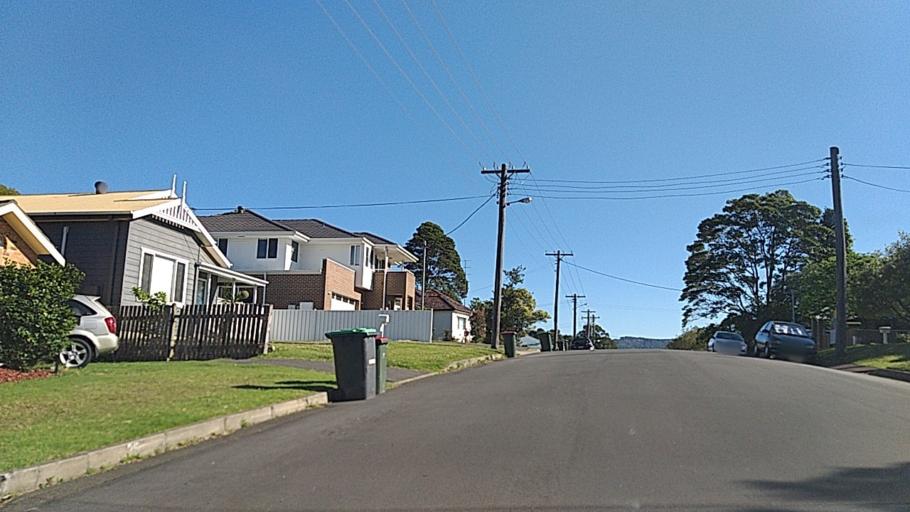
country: AU
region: New South Wales
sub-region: Wollongong
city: Corrimal
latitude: -34.3669
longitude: 150.8930
